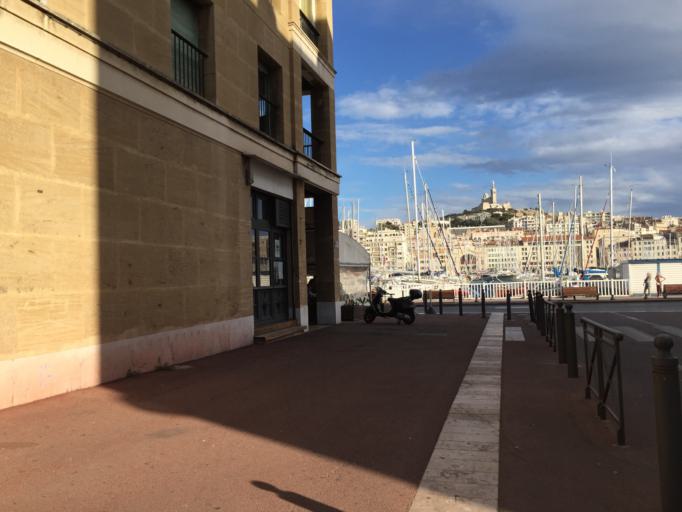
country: FR
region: Provence-Alpes-Cote d'Azur
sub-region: Departement des Bouches-du-Rhone
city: Marseille 02
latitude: 43.2959
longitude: 5.3663
